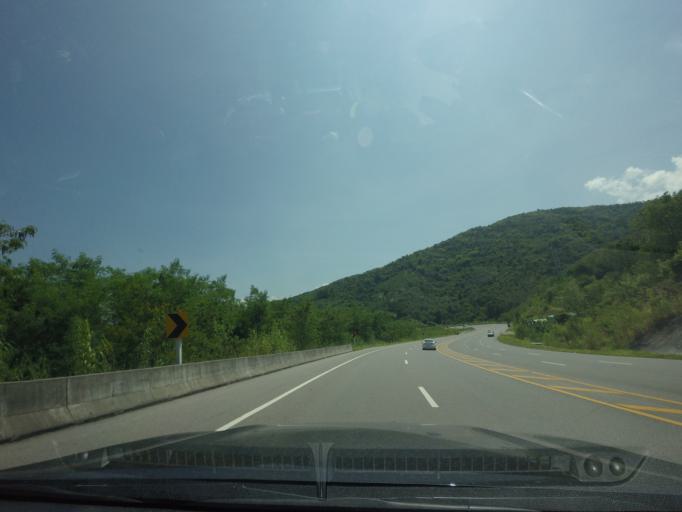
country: TH
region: Phetchabun
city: Lom Sak
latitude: 16.7743
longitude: 101.1212
